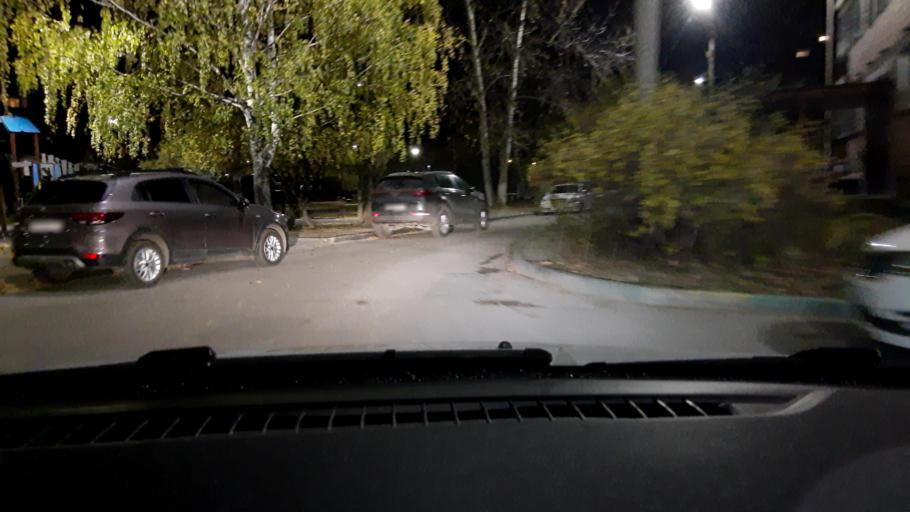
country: RU
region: Nizjnij Novgorod
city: Burevestnik
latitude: 56.2311
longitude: 43.8621
